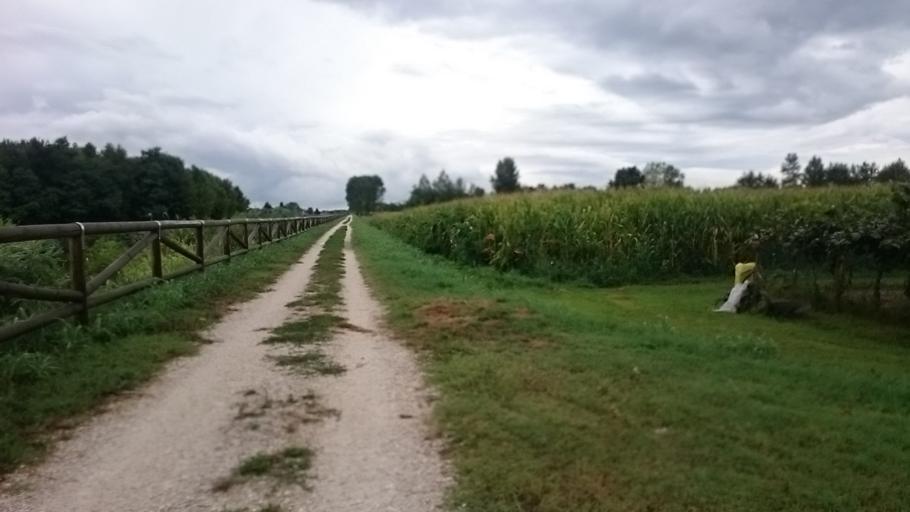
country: IT
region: Veneto
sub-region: Provincia di Padova
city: Loreggiola
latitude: 45.6227
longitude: 11.9268
